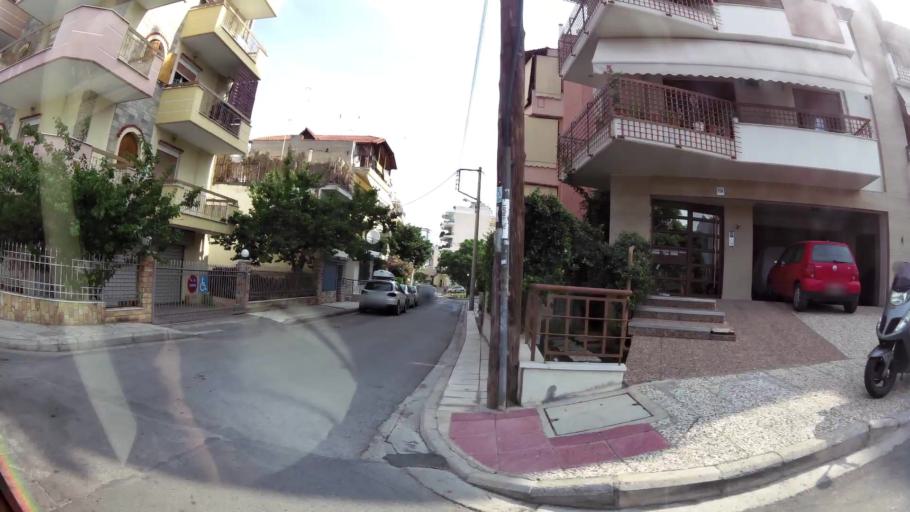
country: GR
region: Central Macedonia
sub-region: Nomos Thessalonikis
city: Sykies
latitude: 40.6575
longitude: 22.9467
